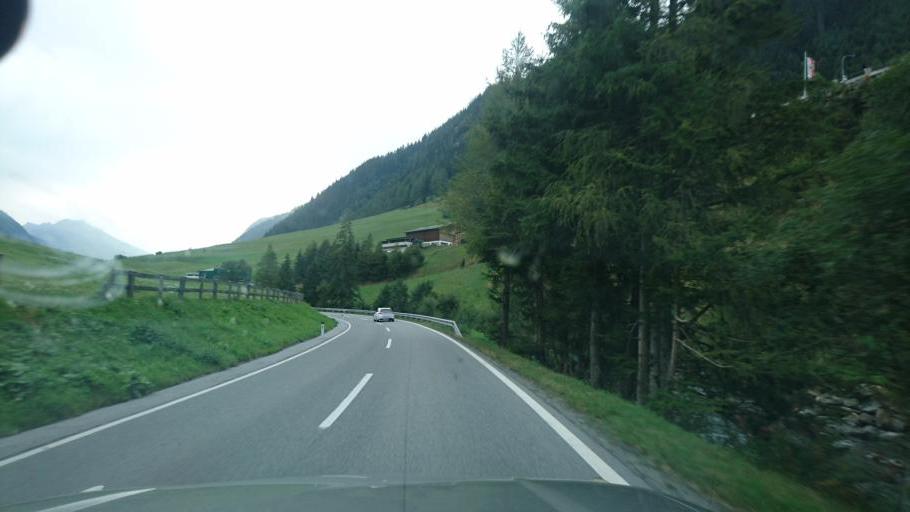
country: AT
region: Tyrol
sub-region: Politischer Bezirk Landeck
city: Ischgl
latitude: 47.0263
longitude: 10.3108
